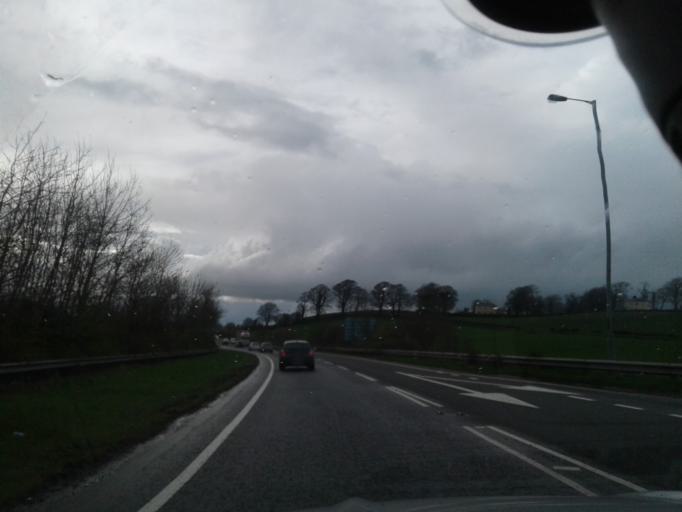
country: GB
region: Northern Ireland
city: Newtownstewart
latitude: 54.7224
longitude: -7.3755
